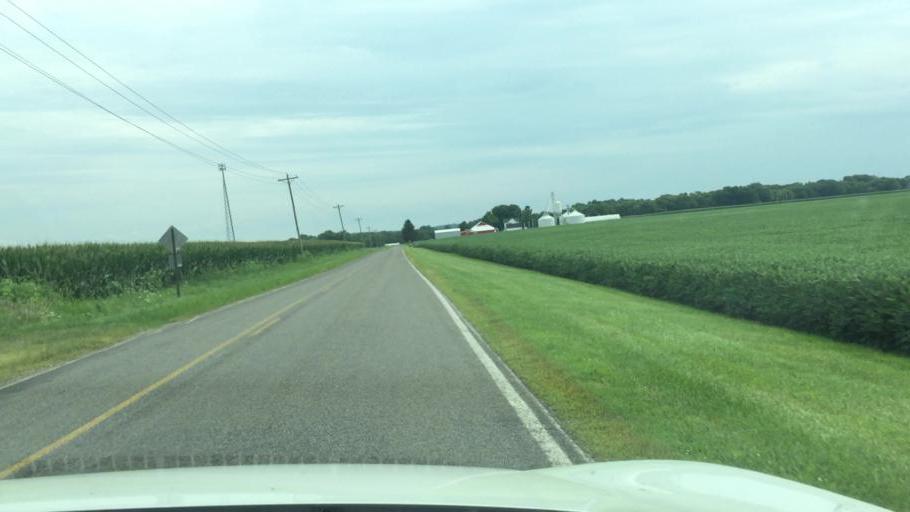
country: US
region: Ohio
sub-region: Champaign County
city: Mechanicsburg
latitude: 40.0382
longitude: -83.6561
